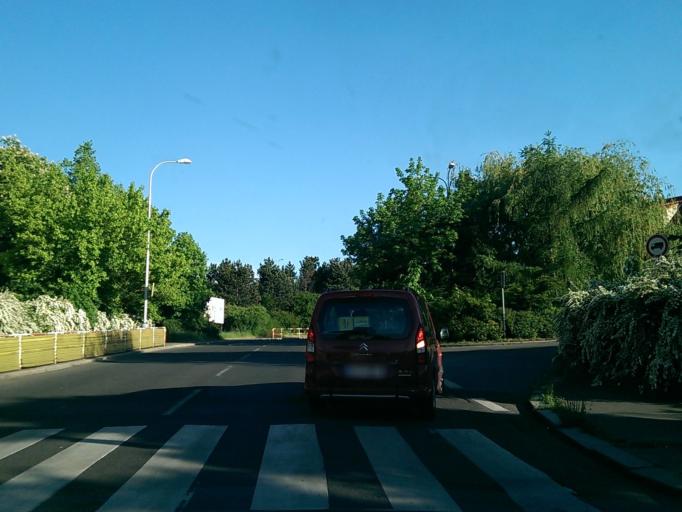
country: CZ
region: Praha
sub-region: Praha 8
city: Karlin
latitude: 50.0430
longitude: 14.4877
